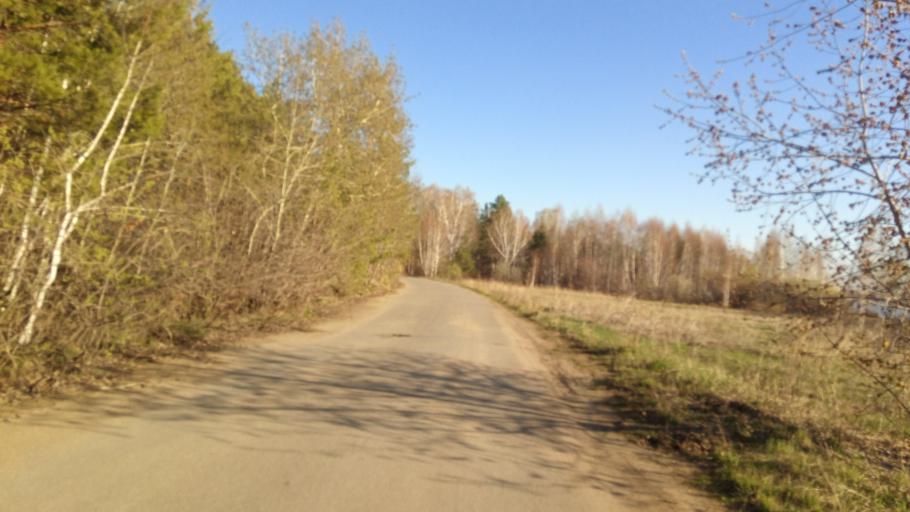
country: RU
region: Chelyabinsk
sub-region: Gorod Chelyabinsk
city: Chelyabinsk
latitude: 55.1347
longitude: 61.3274
